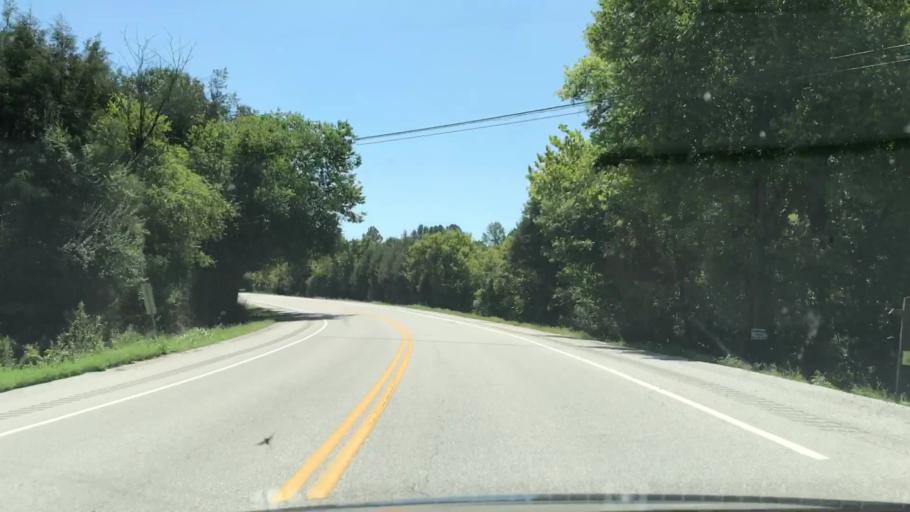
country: US
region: Tennessee
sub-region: Clay County
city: Celina
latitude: 36.4703
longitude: -85.5830
